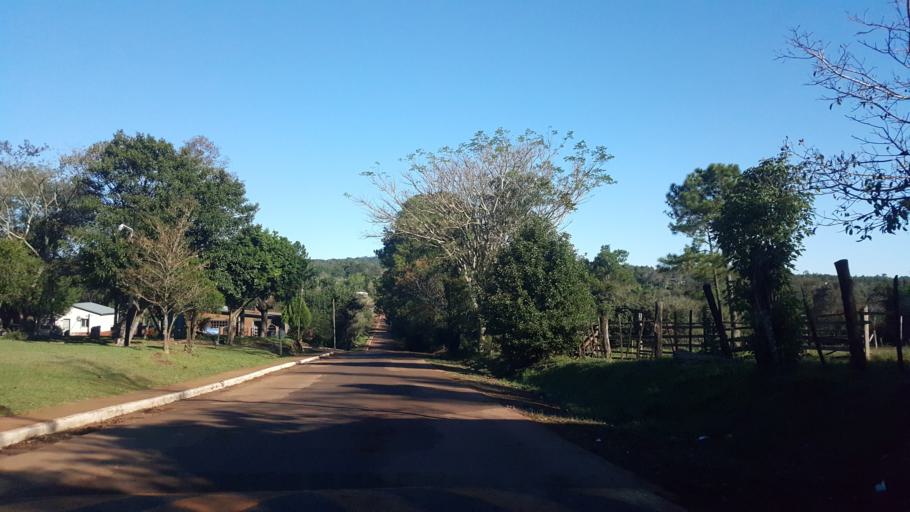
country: AR
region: Misiones
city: Jardin America
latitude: -27.0869
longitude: -55.2864
